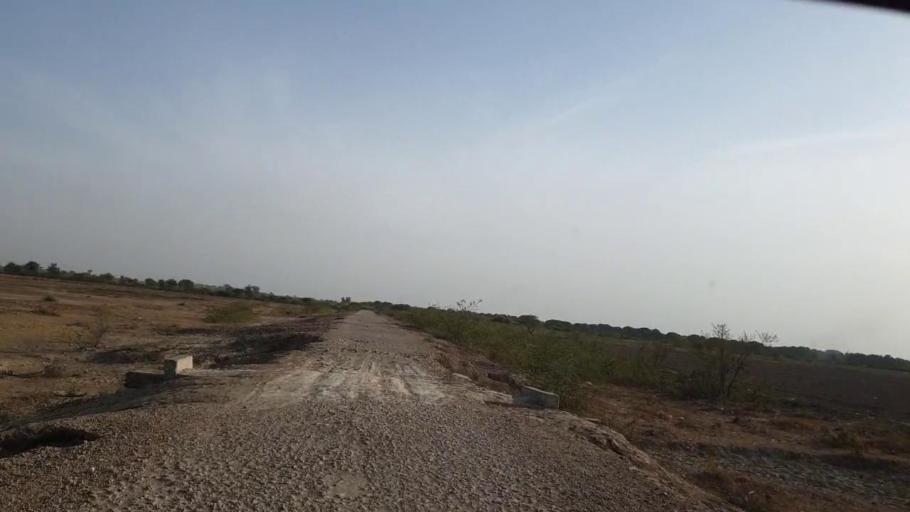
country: PK
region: Sindh
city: Kunri
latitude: 25.0765
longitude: 69.4438
